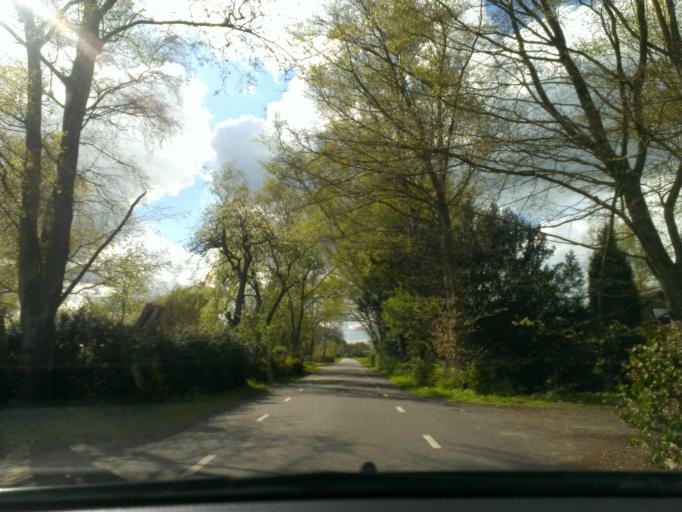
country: NL
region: Gelderland
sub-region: Gemeente Voorst
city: Twello
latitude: 52.2485
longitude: 6.0517
